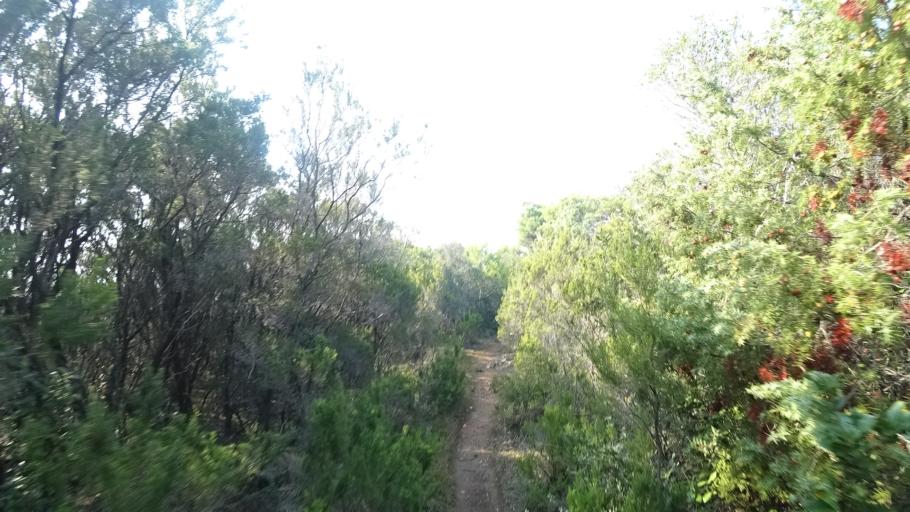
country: HR
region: Primorsko-Goranska
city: Mali Losinj
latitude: 44.4803
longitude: 14.5122
